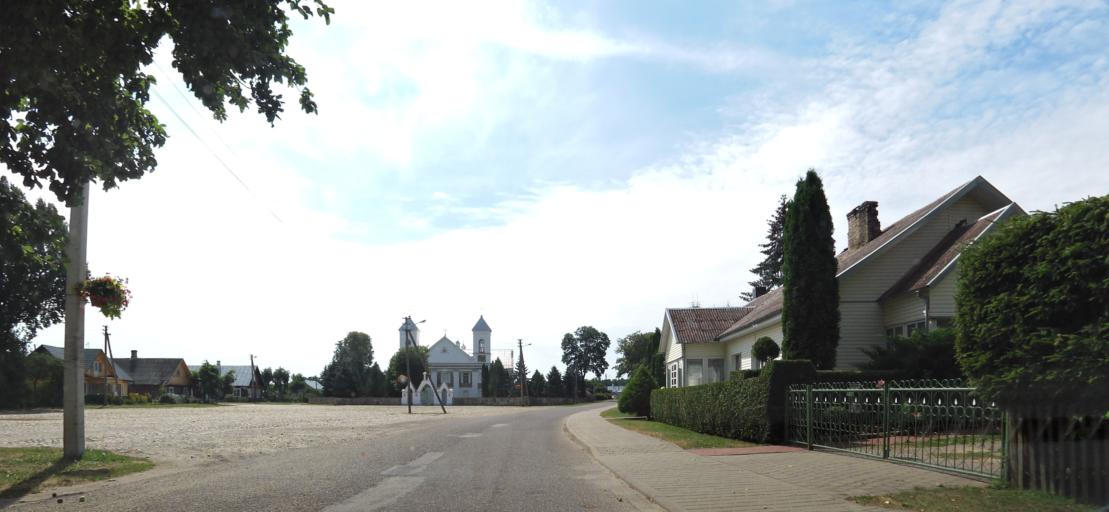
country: LT
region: Vilnius County
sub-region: Trakai
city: Rudiskes
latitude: 54.3593
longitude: 24.8404
